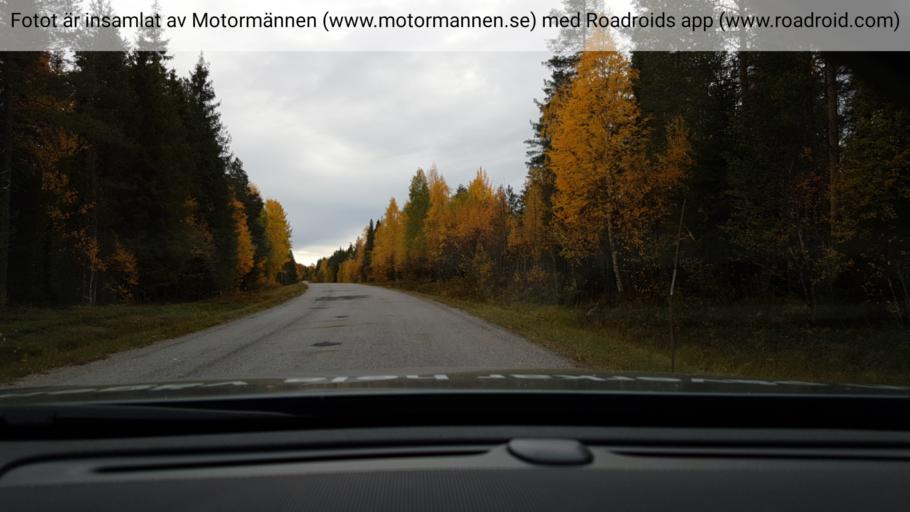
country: SE
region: Norrbotten
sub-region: Overkalix Kommun
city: OEverkalix
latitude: 66.2441
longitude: 23.0027
